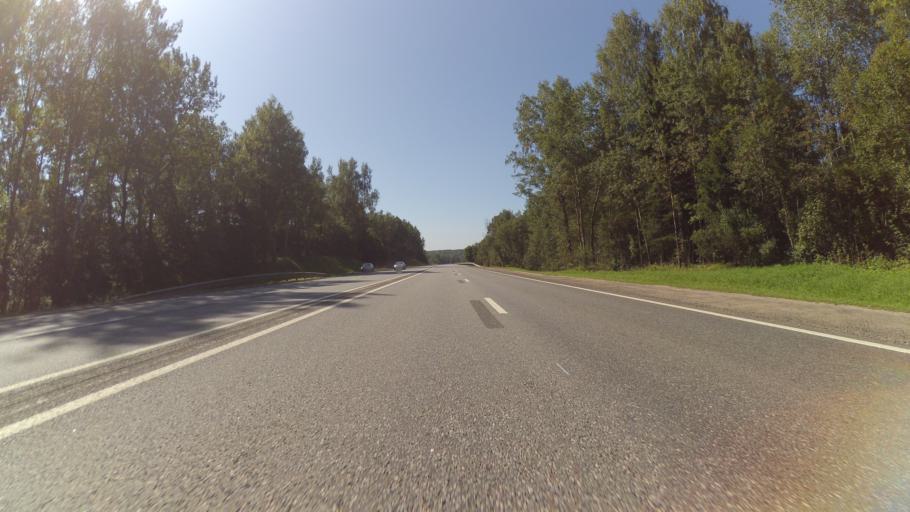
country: RU
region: Smolensk
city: Pechersk
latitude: 54.9044
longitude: 32.1219
